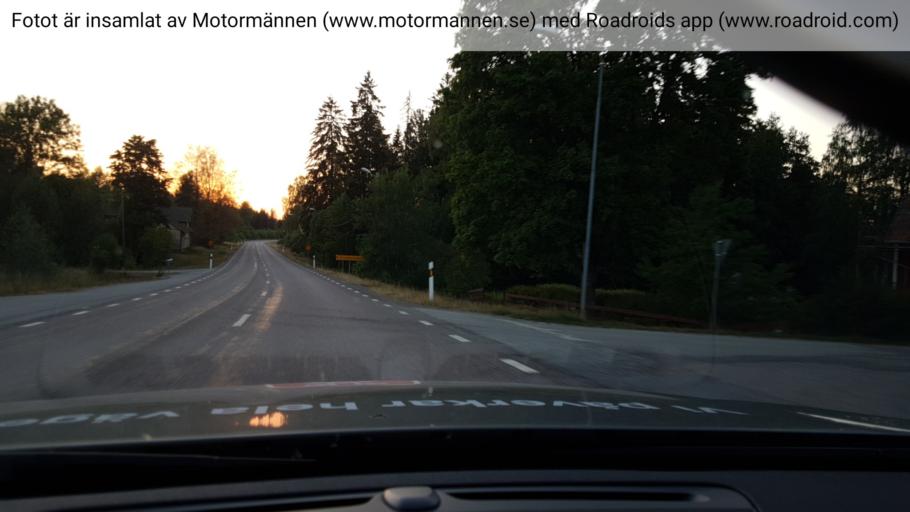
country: SE
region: Uppsala
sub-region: Heby Kommun
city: OEstervala
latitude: 60.0772
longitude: 17.1994
